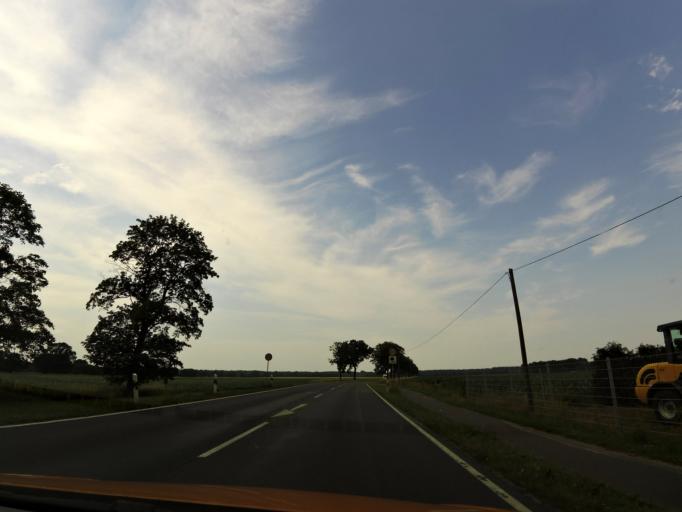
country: DE
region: Brandenburg
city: Wusterhausen
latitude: 52.8992
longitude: 12.4507
